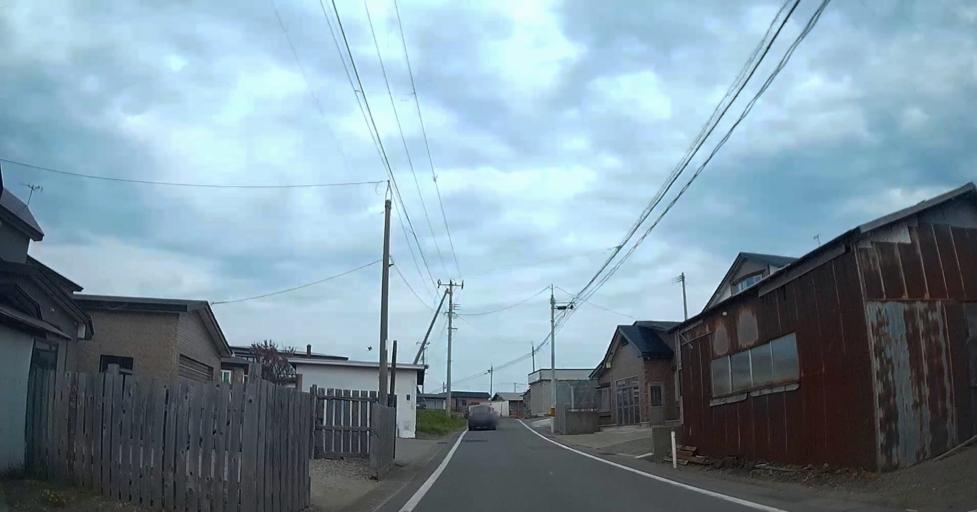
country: JP
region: Aomori
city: Shimokizukuri
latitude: 41.0257
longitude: 140.3272
